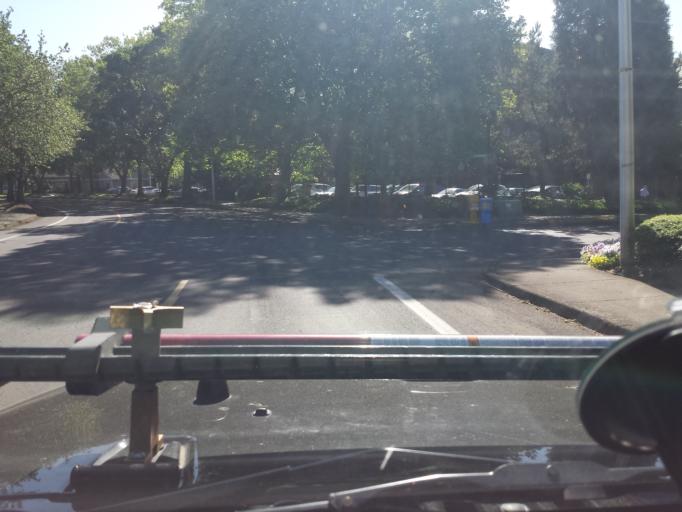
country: US
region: Washington
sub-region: Clark County
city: Walnut Grove
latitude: 45.6544
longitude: -122.5928
